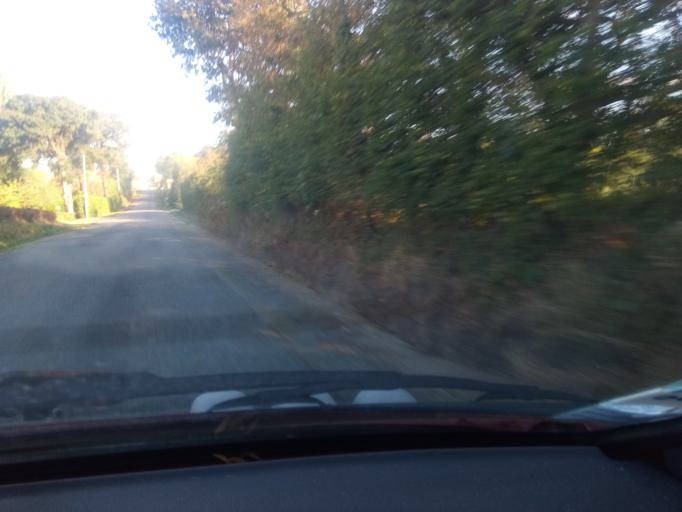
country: FR
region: Poitou-Charentes
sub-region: Departement de la Vienne
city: Availles-Limouzine
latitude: 46.1263
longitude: 0.7237
